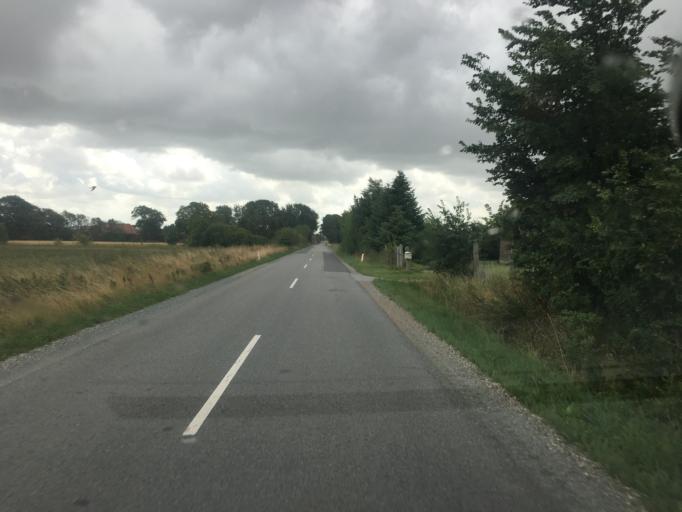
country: DK
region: South Denmark
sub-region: Tonder Kommune
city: Logumkloster
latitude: 54.9958
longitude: 8.9625
